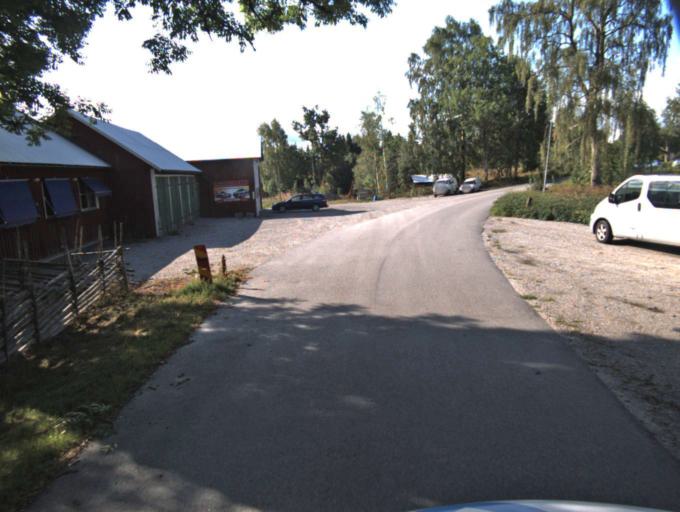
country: SE
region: Vaestra Goetaland
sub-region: Ulricehamns Kommun
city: Ulricehamn
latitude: 57.6755
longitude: 13.4720
